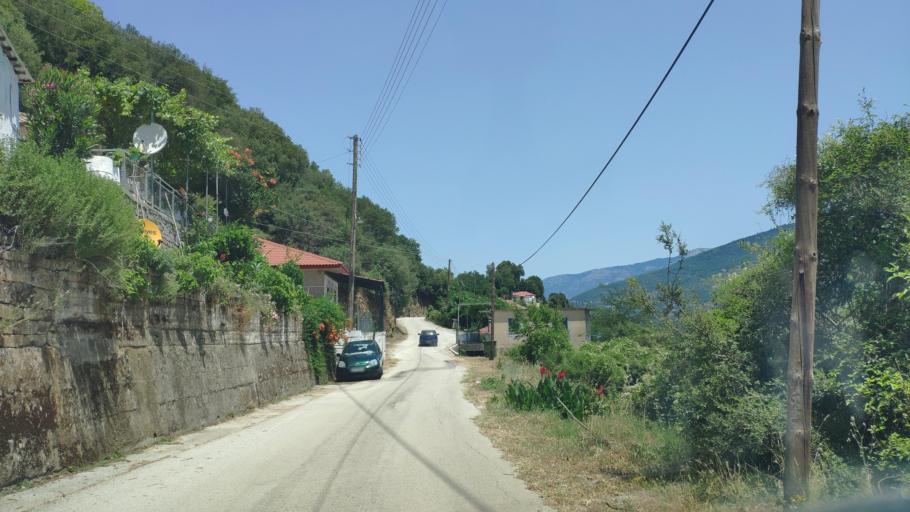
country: GR
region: Epirus
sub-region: Nomos Artas
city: Ano Kalentini
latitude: 39.2060
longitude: 21.3428
